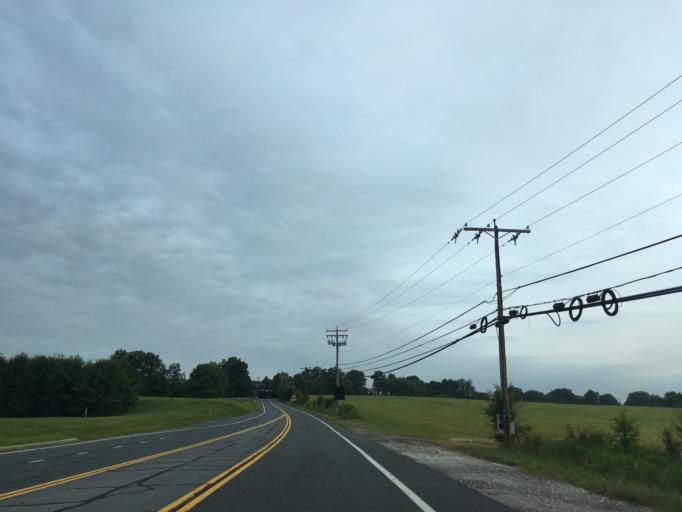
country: US
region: Maryland
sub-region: Howard County
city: Columbia
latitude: 39.3148
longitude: -76.8801
